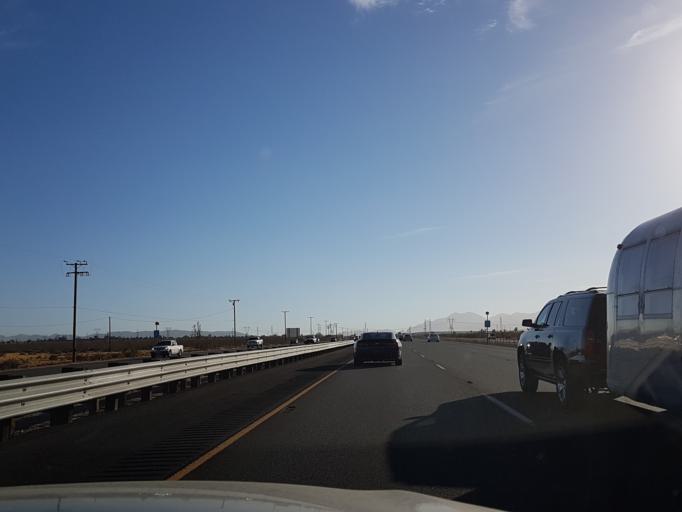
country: US
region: California
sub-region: San Bernardino County
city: Mountain View Acres
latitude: 34.4580
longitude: -117.3561
